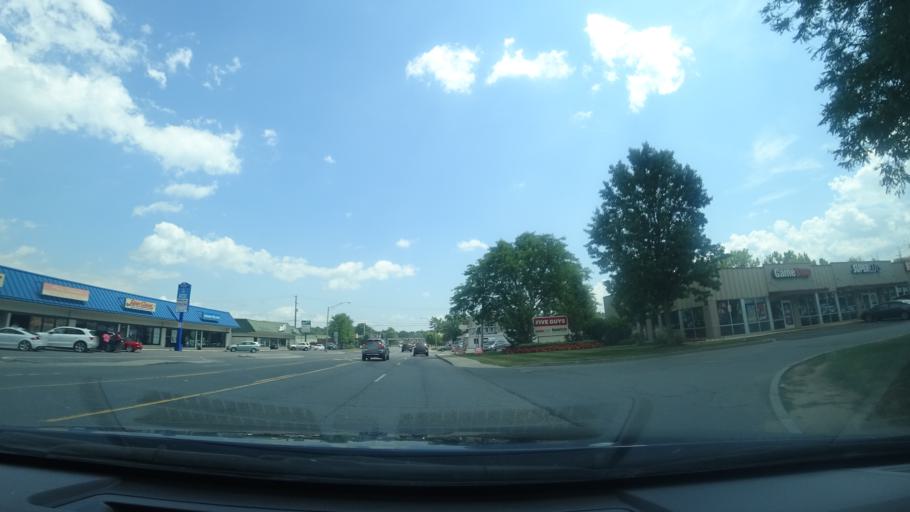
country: US
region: New York
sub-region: Warren County
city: Glens Falls North
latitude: 43.3285
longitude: -73.6698
